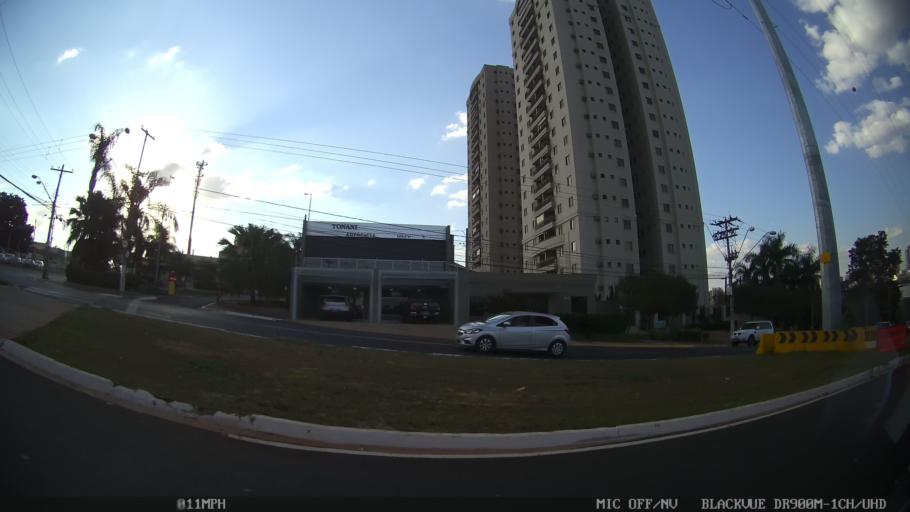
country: BR
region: Sao Paulo
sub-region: Ribeirao Preto
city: Ribeirao Preto
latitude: -21.1932
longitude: -47.7998
